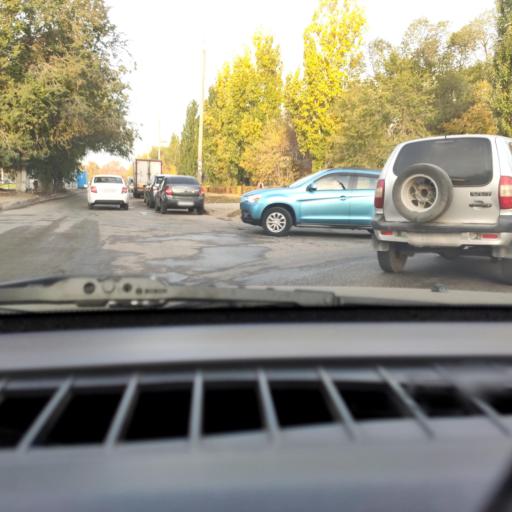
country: RU
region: Samara
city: Tol'yatti
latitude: 53.5284
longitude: 49.2919
